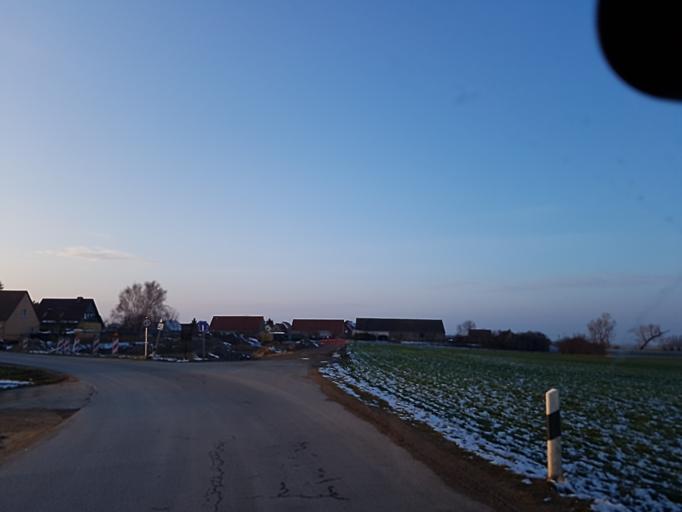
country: DE
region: Saxony
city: Strehla
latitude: 51.3869
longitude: 13.2068
